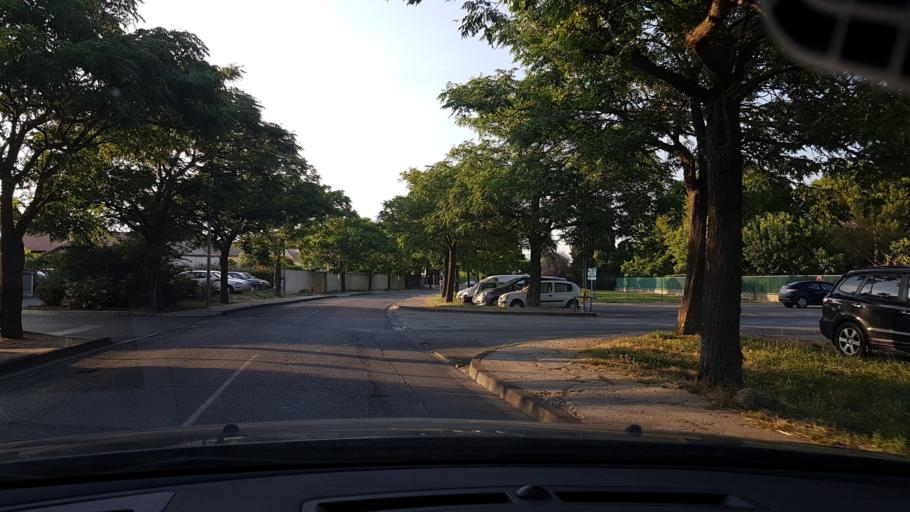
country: FR
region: Provence-Alpes-Cote d'Azur
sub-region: Departement du Vaucluse
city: Carpentras
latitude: 44.0454
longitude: 5.0533
